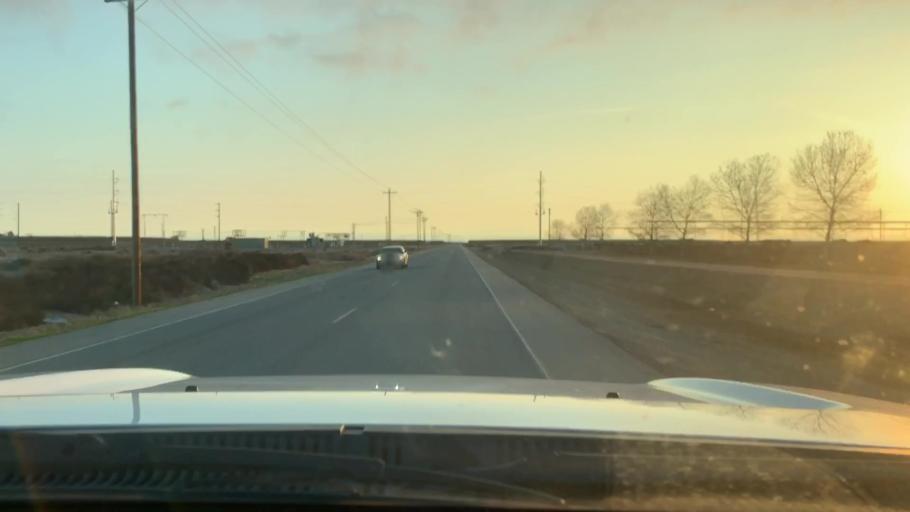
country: US
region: California
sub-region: Kern County
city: Buttonwillow
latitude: 35.5005
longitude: -119.4518
